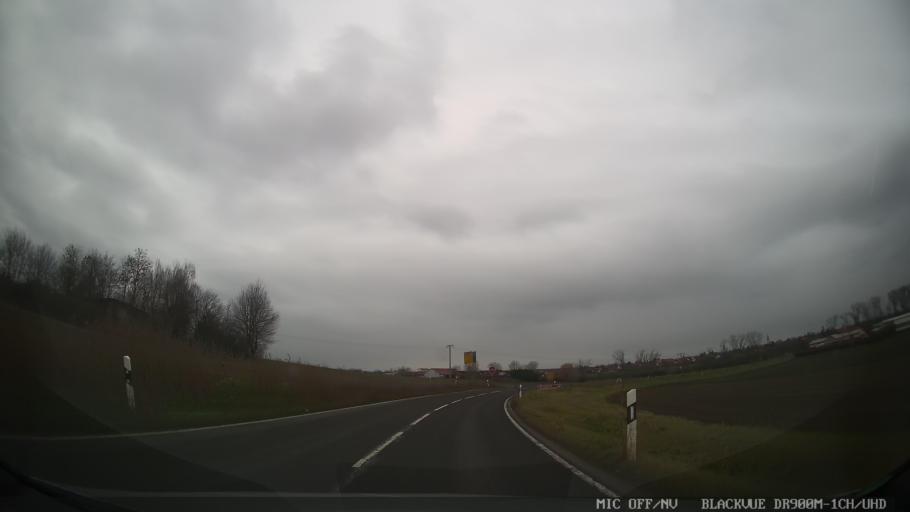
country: DE
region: Rheinland-Pfalz
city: Gau-Odernheim
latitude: 49.7753
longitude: 8.2043
